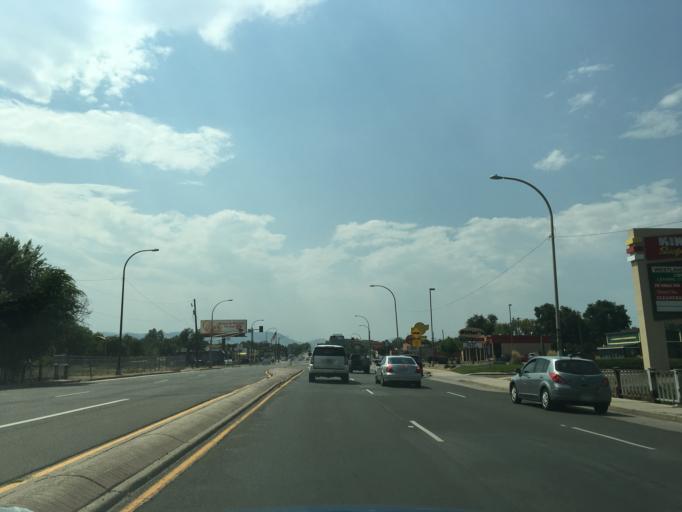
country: US
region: Colorado
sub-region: Jefferson County
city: Applewood
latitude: 39.7402
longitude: -105.1245
